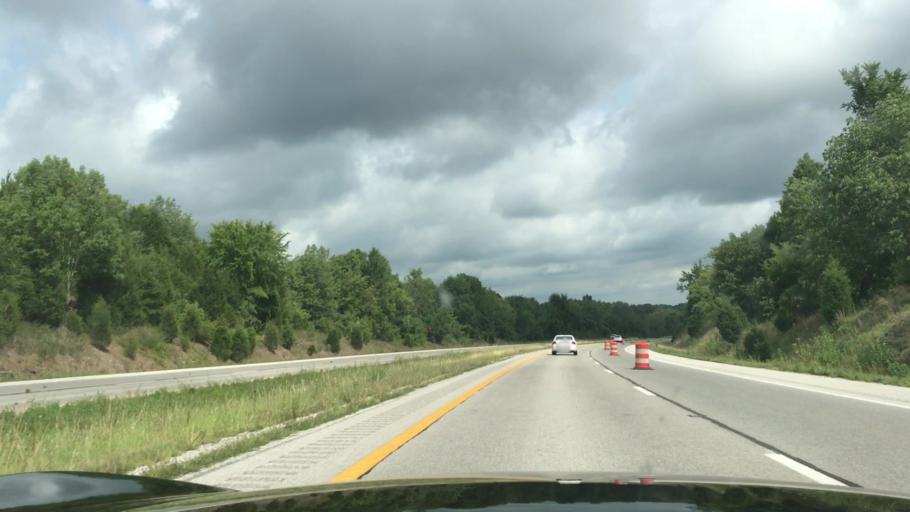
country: US
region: Kentucky
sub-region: Butler County
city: Morgantown
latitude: 37.1023
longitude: -86.6391
